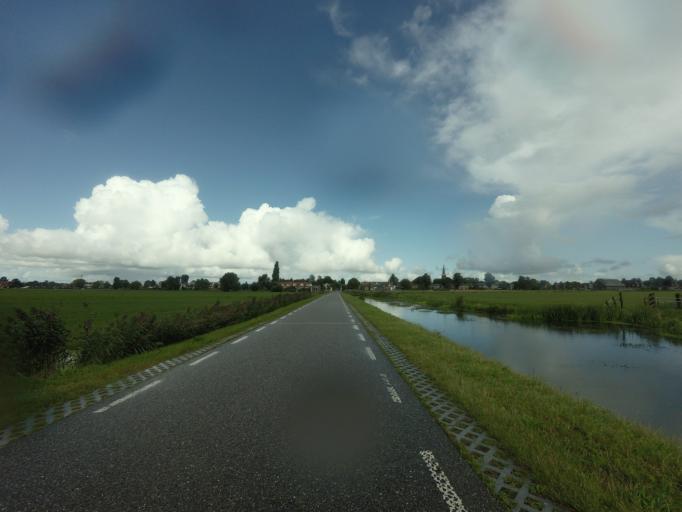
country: NL
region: Friesland
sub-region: Gemeente Leeuwarden
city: Wirdum
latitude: 53.1451
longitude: 5.8031
